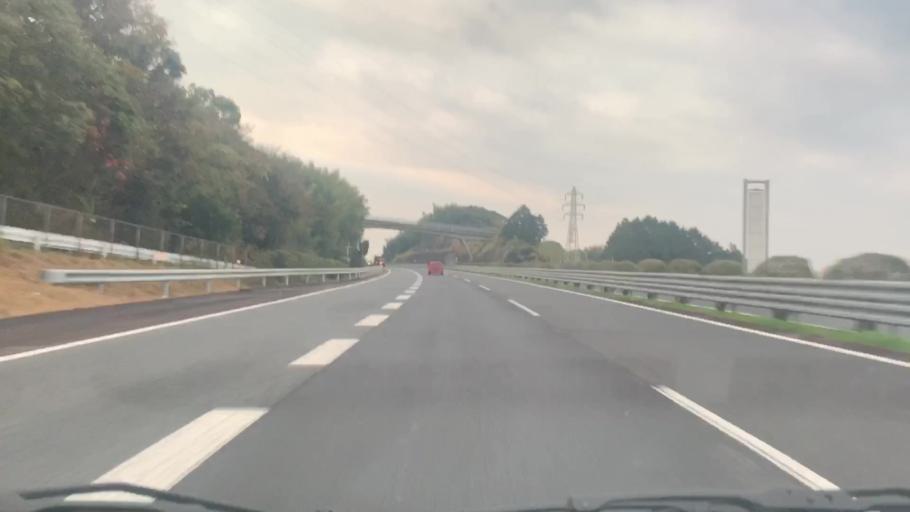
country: JP
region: Nagasaki
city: Omura
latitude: 32.9954
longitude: 129.9520
